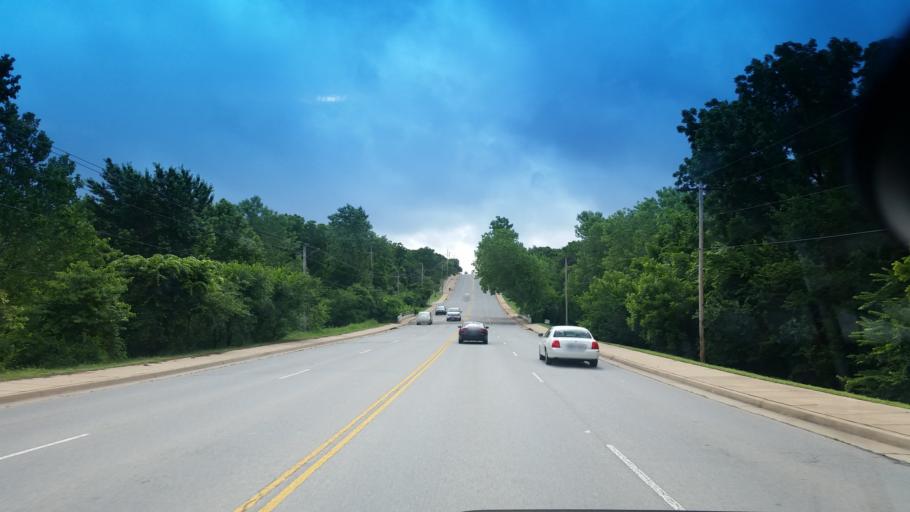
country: US
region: Oklahoma
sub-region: Oklahoma County
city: Edmond
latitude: 35.6383
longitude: -97.4413
